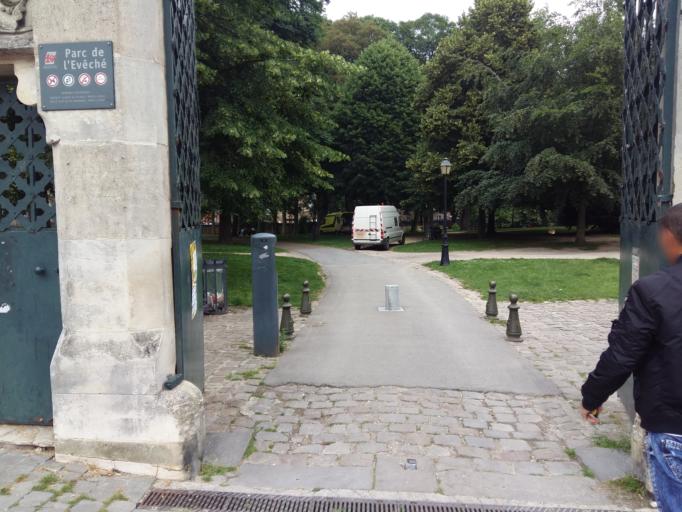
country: FR
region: Picardie
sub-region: Departement de la Somme
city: Amiens
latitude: 49.8941
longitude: 2.3034
